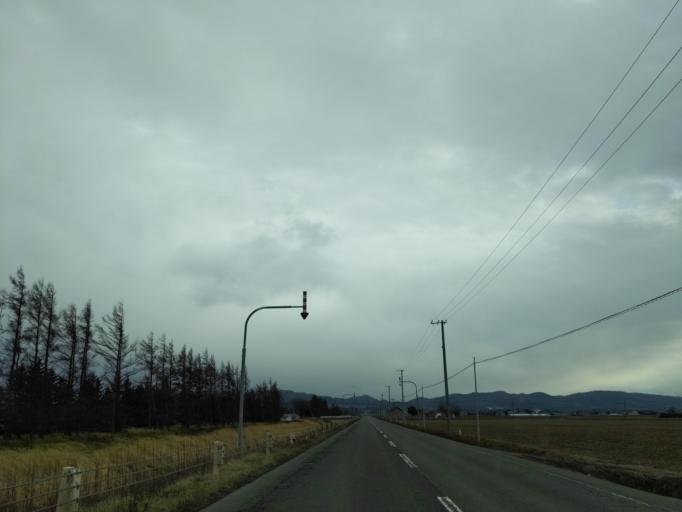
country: JP
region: Hokkaido
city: Kitahiroshima
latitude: 43.0409
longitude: 141.6866
